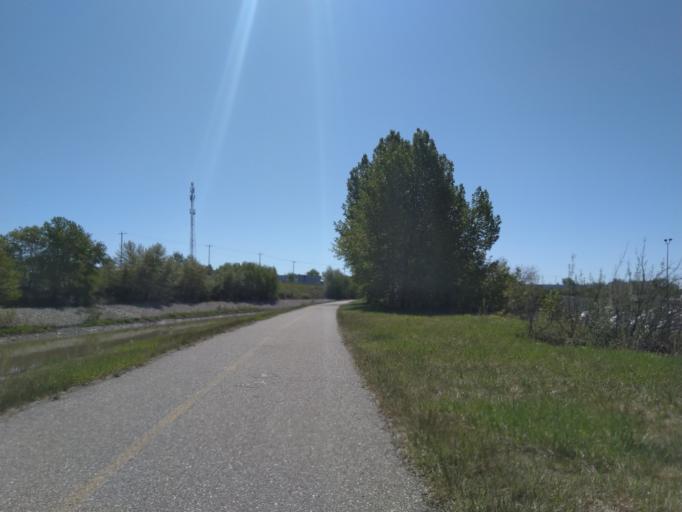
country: CA
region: Alberta
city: Calgary
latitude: 50.9956
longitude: -113.9896
